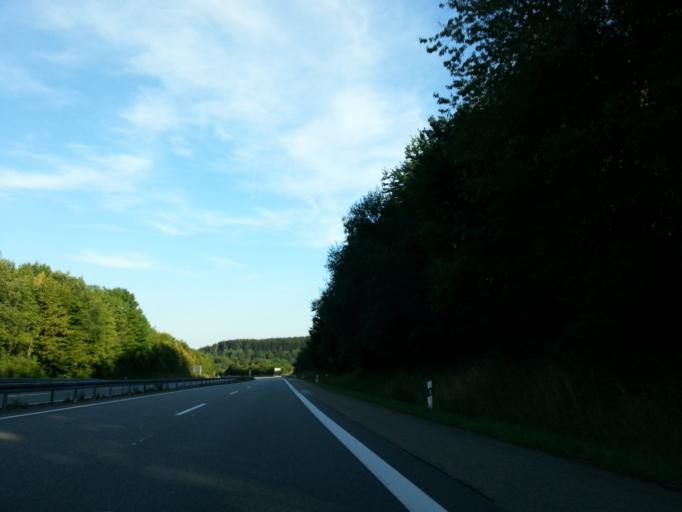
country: DE
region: Rheinland-Pfalz
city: Achtelsbach
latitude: 49.5924
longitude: 7.0557
